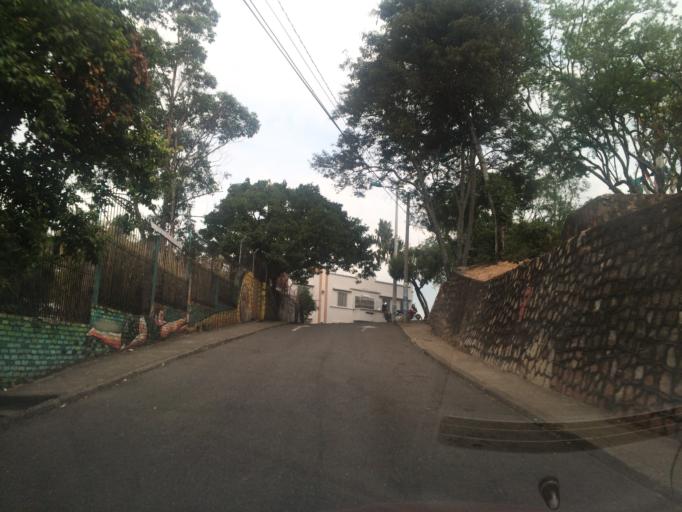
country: CO
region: Valle del Cauca
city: Cali
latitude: 3.4474
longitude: -76.5407
